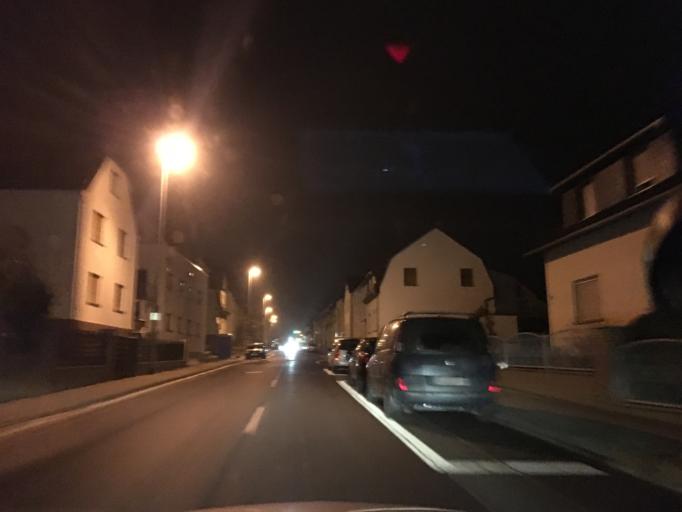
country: DE
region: Hesse
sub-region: Regierungsbezirk Darmstadt
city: Hofheim am Taunus
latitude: 50.0599
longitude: 8.4154
